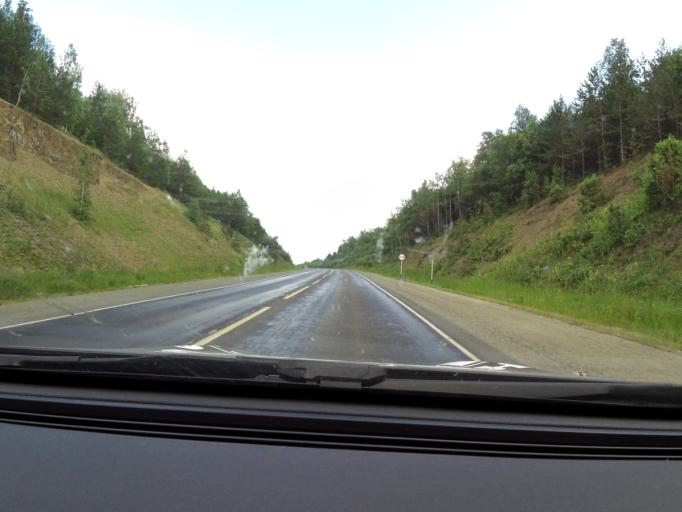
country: RU
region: Sverdlovsk
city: Bisert'
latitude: 56.8347
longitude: 58.8890
